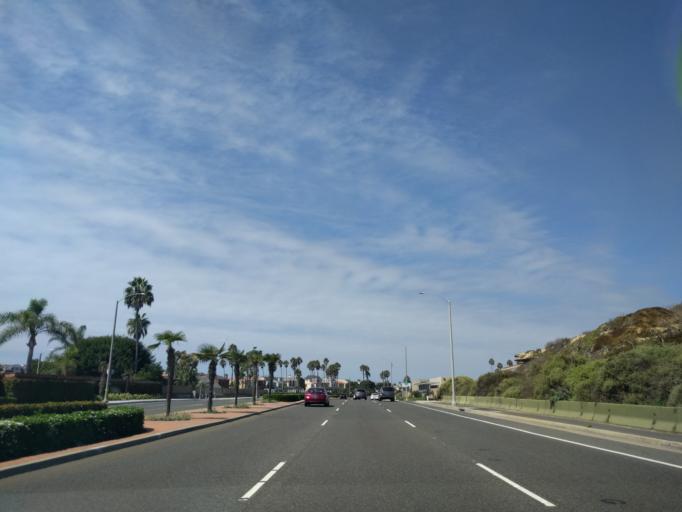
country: US
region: California
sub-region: Orange County
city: Newport Beach
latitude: 33.6252
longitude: -117.9449
